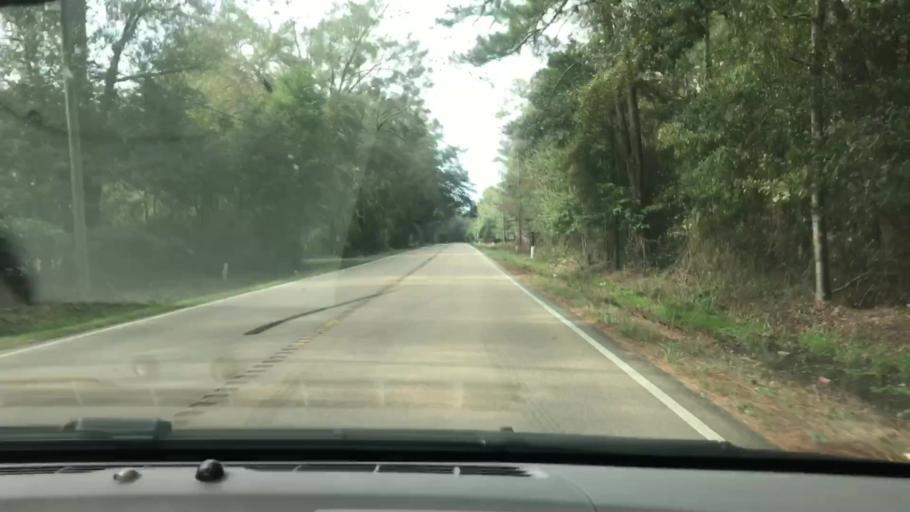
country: US
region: Louisiana
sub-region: Saint Tammany Parish
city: Abita Springs
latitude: 30.4935
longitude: -90.0110
